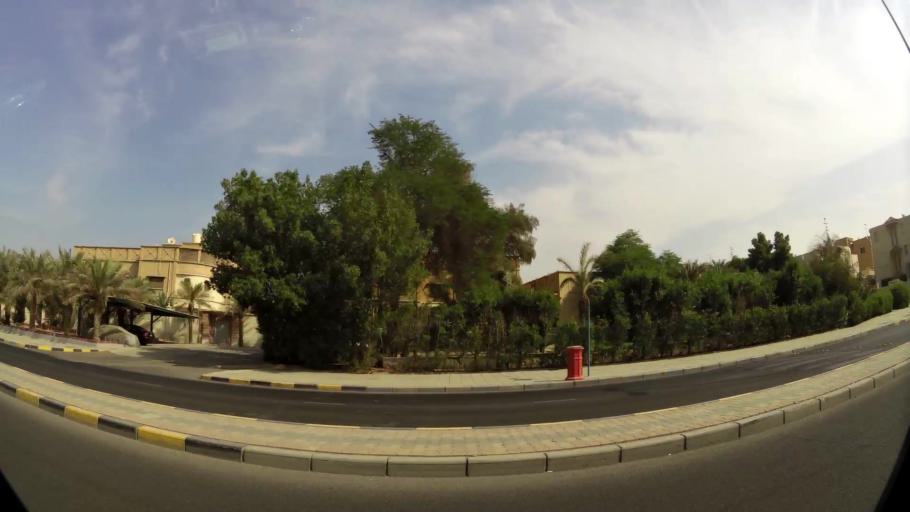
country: KW
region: Al Asimah
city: Ash Shamiyah
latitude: 29.3481
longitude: 47.9679
